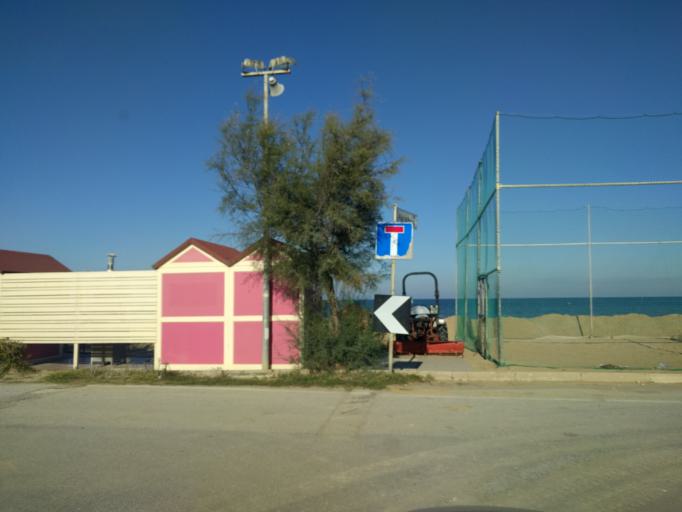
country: IT
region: The Marches
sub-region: Provincia di Pesaro e Urbino
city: Marotta
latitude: 43.7872
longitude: 13.1127
